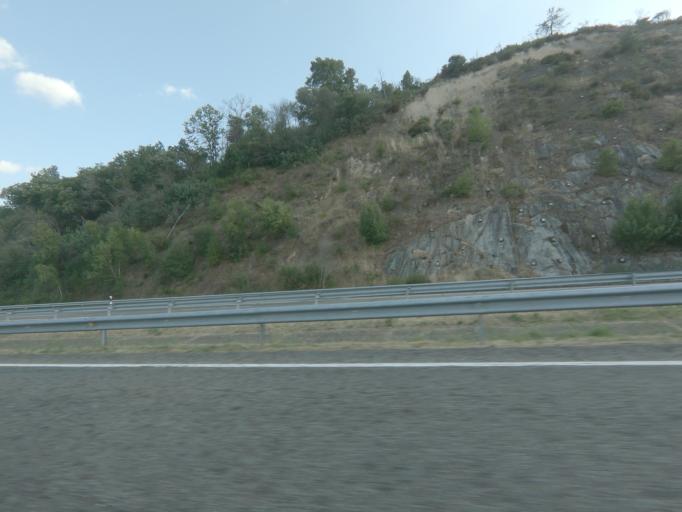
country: ES
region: Galicia
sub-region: Provincia de Ourense
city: Oimbra
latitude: 41.9247
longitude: -7.4842
